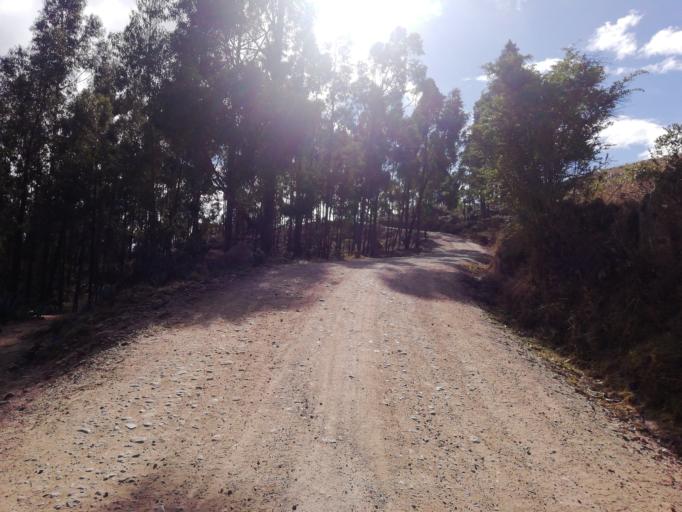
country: CO
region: Boyaca
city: Gameza
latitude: 5.8093
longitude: -72.8115
